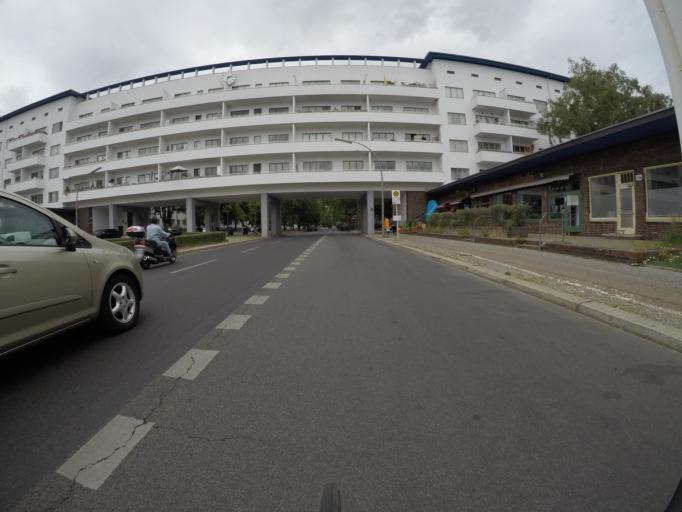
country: DE
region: Berlin
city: Reinickendorf
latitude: 52.5699
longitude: 13.3514
